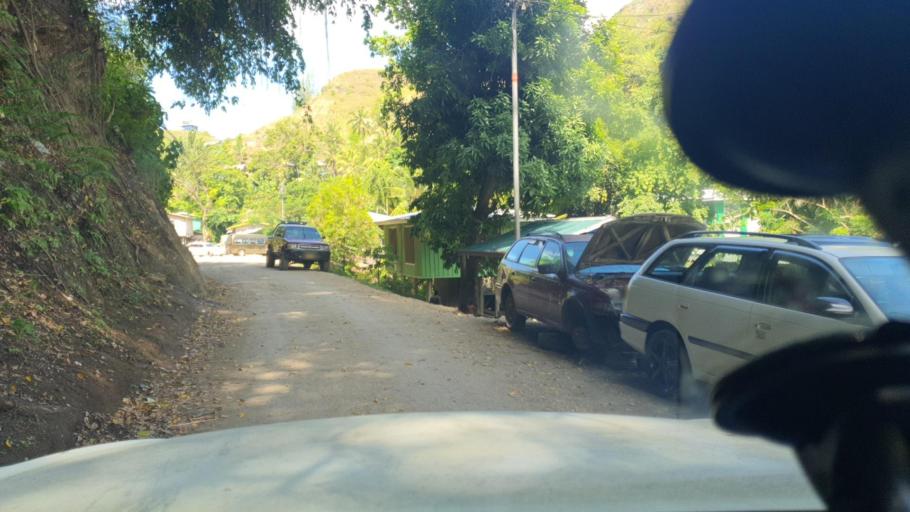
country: SB
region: Guadalcanal
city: Honiara
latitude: -9.4475
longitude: 159.9616
